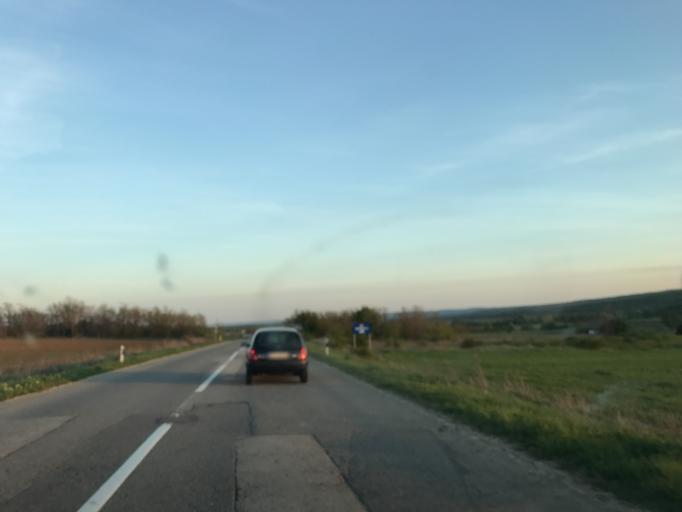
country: RO
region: Mehedinti
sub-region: Comuna Gogosu
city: Ostrovu Mare
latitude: 44.3092
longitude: 22.5044
